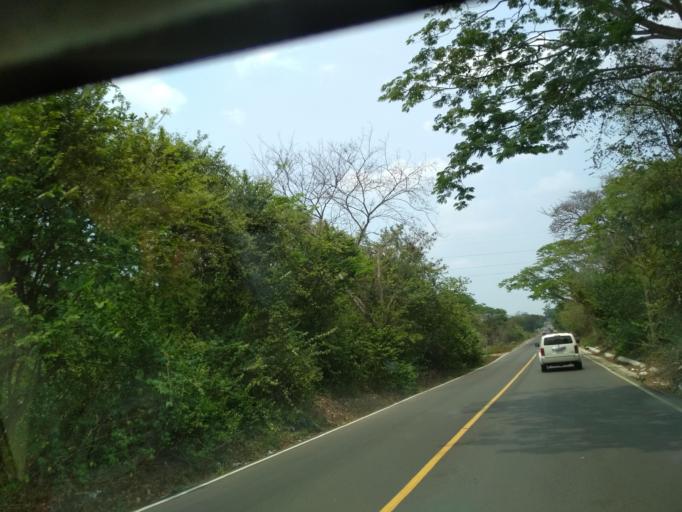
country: MX
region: Veracruz
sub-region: Veracruz
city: Delfino Victoria (Santa Fe)
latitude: 19.1705
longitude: -96.2818
